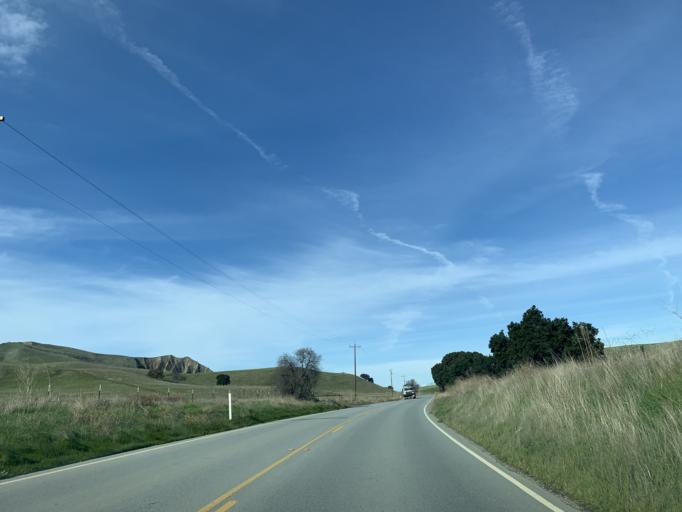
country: US
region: California
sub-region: San Benito County
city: Ridgemark
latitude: 36.7483
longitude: -121.2862
